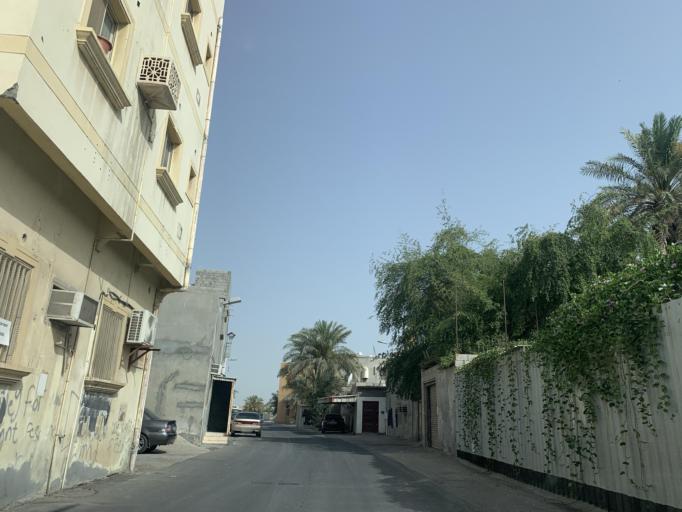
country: BH
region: Northern
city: Sitrah
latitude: 26.1348
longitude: 50.5969
